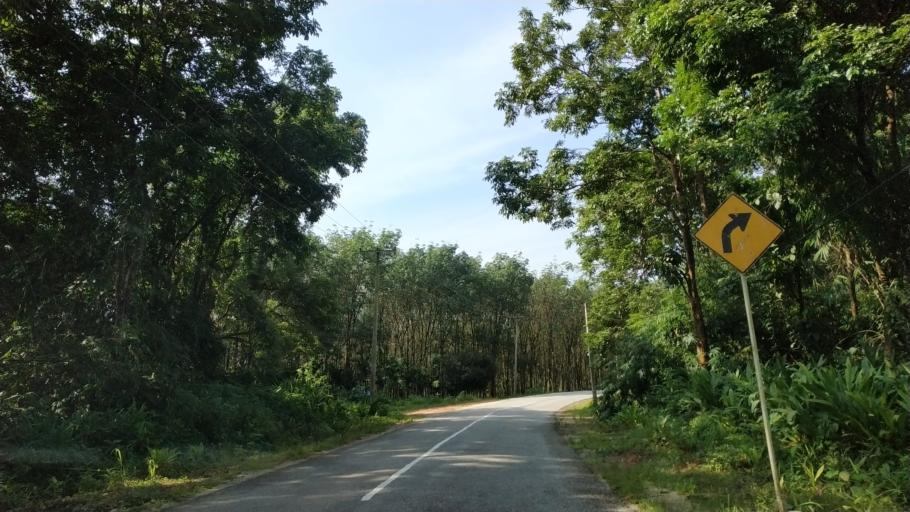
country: TH
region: Kanchanaburi
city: Thong Pha Phum
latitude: 14.6191
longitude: 98.1135
